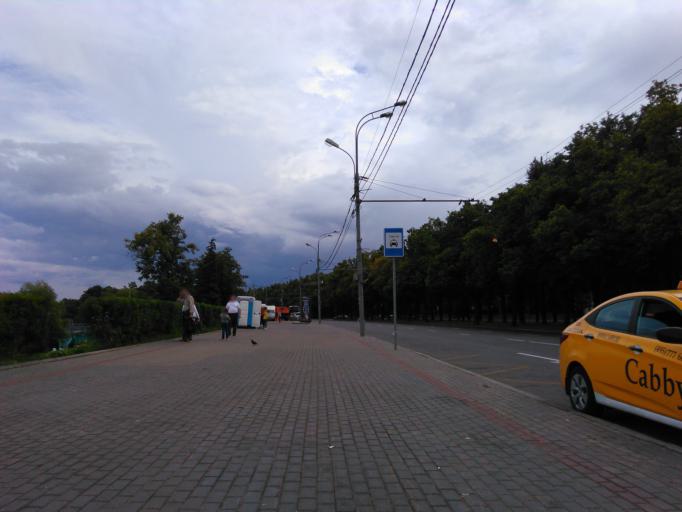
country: RU
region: Moscow
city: Luzhniki
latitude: 55.7085
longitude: 37.5436
